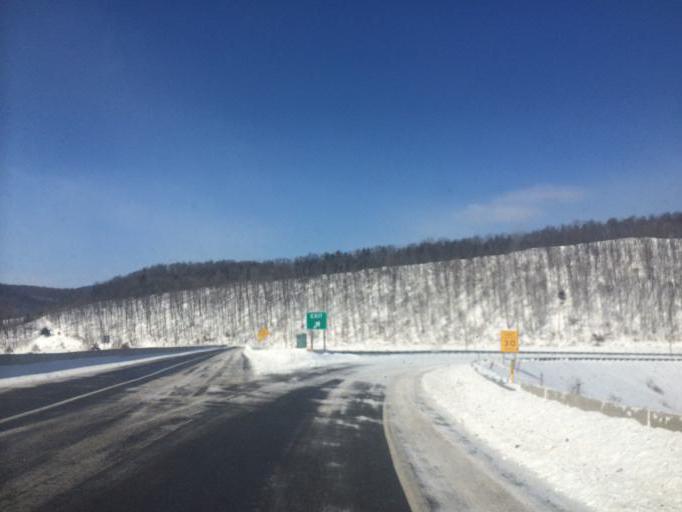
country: US
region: Pennsylvania
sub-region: Centre County
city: Stormstown
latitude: 40.8285
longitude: -78.0145
